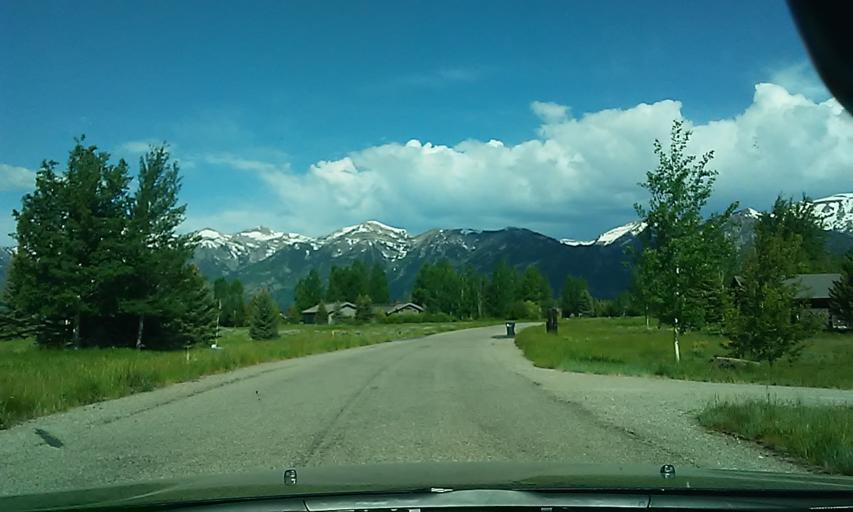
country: US
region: Wyoming
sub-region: Teton County
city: Jackson
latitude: 43.5775
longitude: -110.7547
